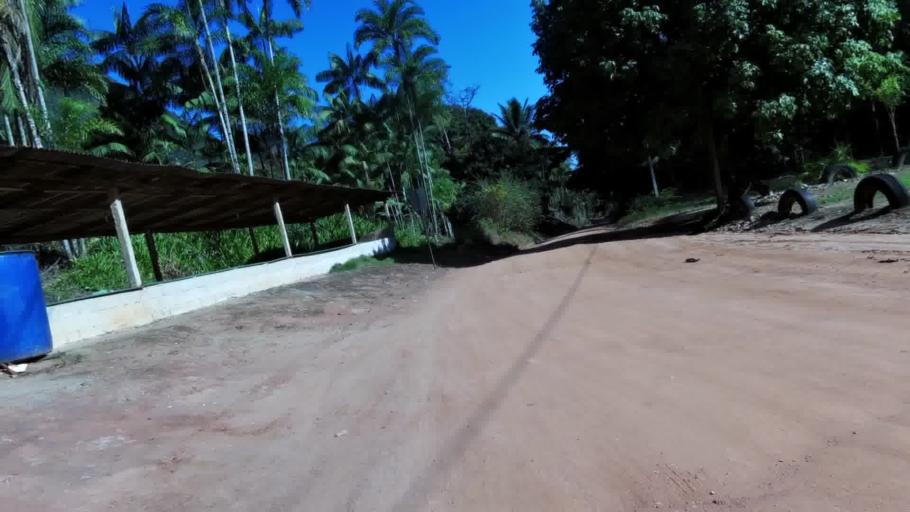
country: BR
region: Espirito Santo
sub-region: Alfredo Chaves
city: Alfredo Chaves
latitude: -20.5497
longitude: -40.7255
